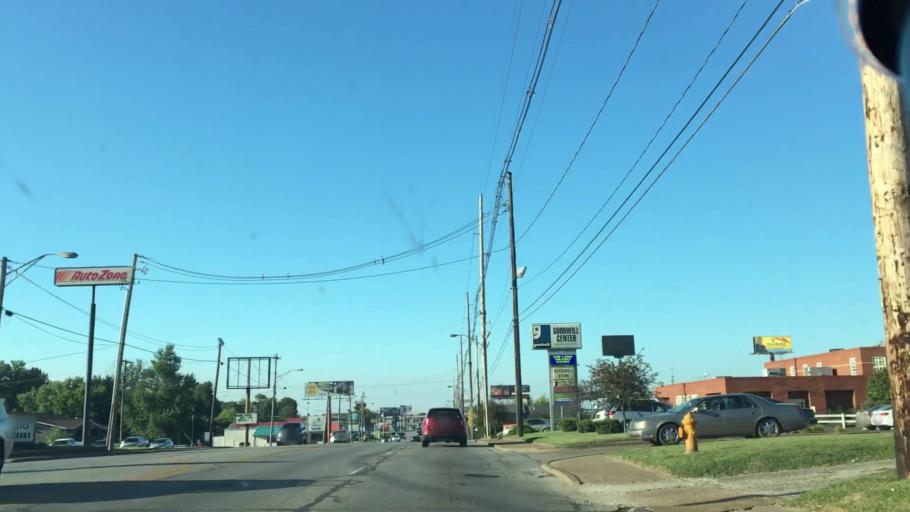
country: US
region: Indiana
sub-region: Vanderburgh County
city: Melody Hill
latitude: 37.9705
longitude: -87.4926
